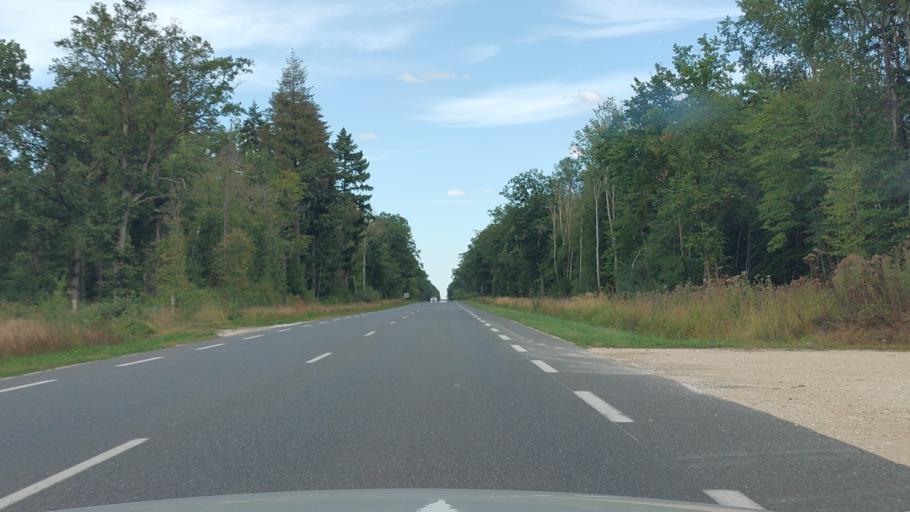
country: FR
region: Ile-de-France
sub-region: Departement de Seine-et-Marne
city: La Chapelle-Gauthier
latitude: 48.5448
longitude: 2.8408
